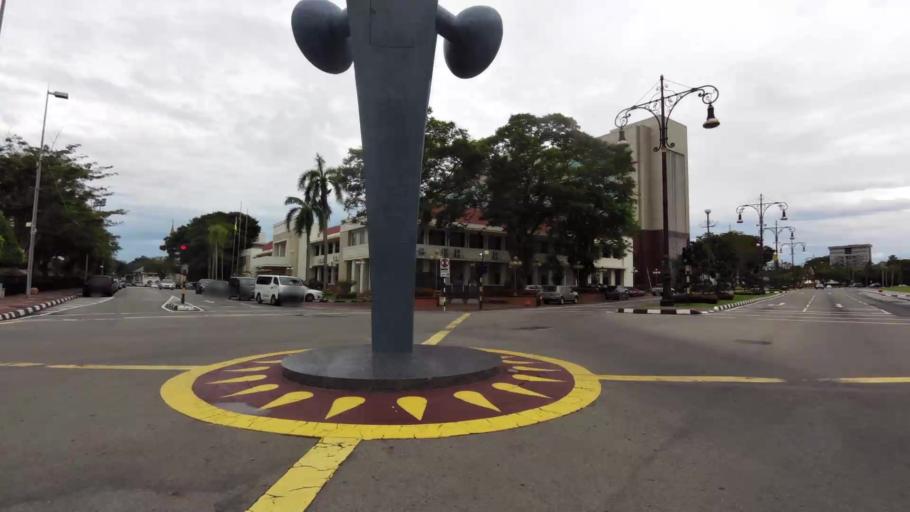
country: BN
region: Brunei and Muara
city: Bandar Seri Begawan
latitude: 4.8903
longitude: 114.9425
